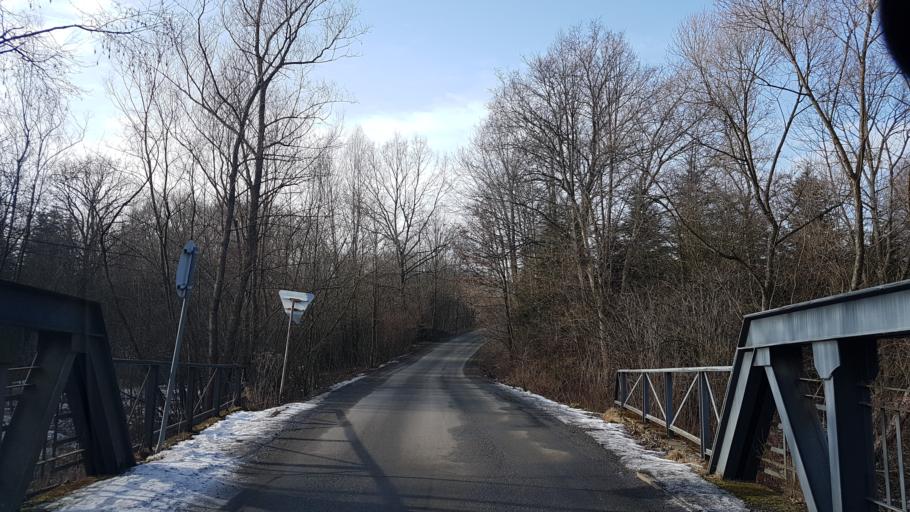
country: PL
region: Lesser Poland Voivodeship
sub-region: Powiat limanowski
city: Lukowica
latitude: 49.6620
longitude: 20.4853
